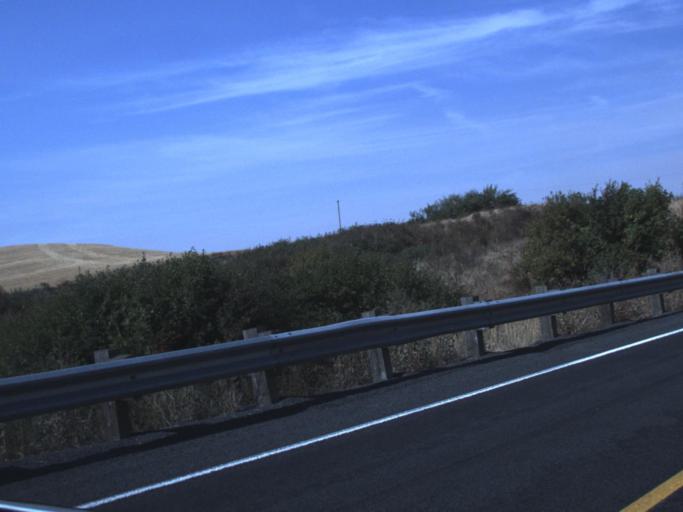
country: US
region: Washington
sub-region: Whitman County
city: Pullman
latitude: 46.9813
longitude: -117.1254
